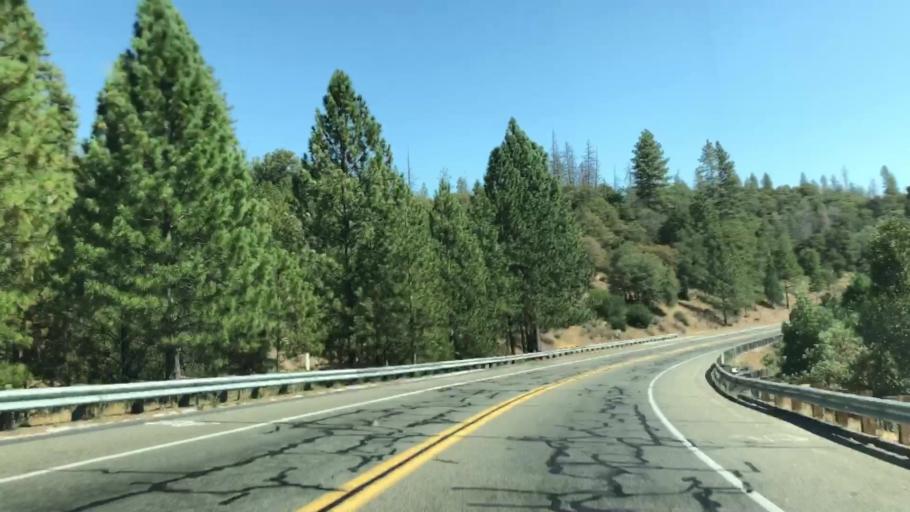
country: US
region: California
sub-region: Tuolumne County
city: Tuolumne City
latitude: 37.8387
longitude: -120.2068
